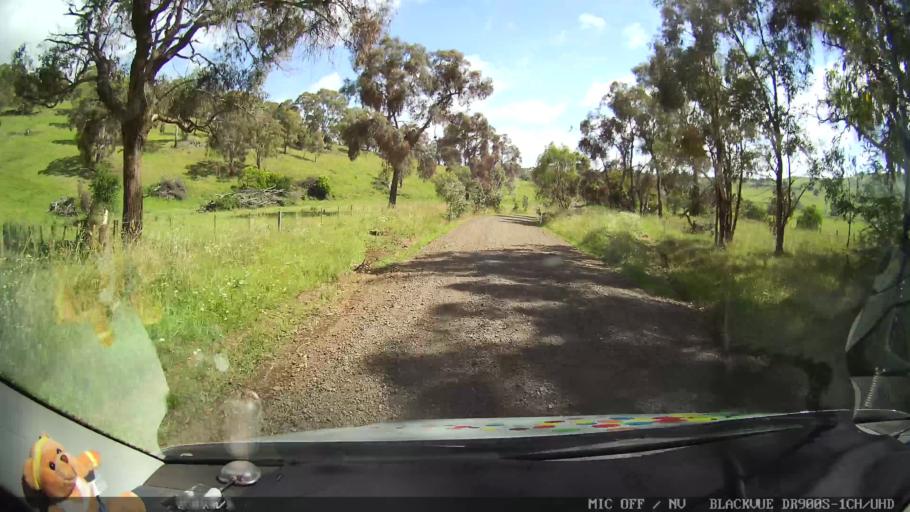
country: AU
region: New South Wales
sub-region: Guyra
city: Guyra
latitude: -29.9840
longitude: 151.6946
